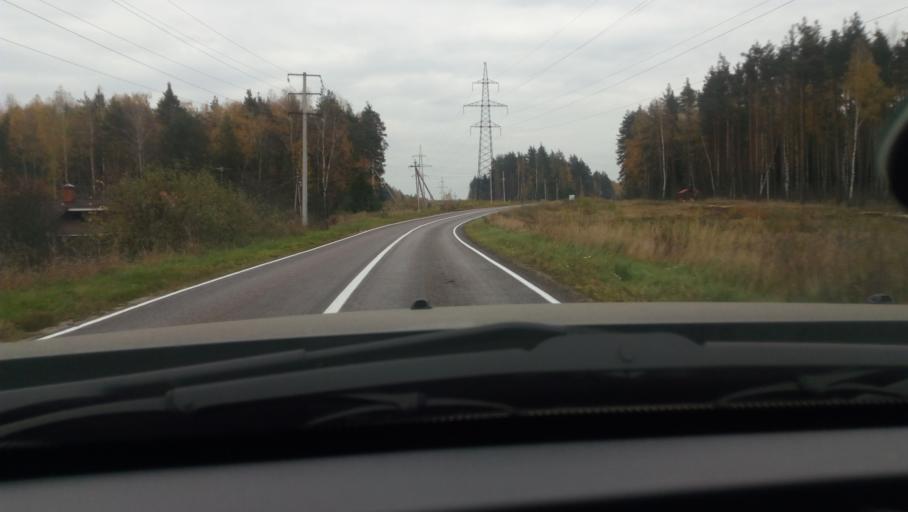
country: RU
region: Moskovskaya
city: Avsyunino
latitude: 55.6040
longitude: 39.1998
